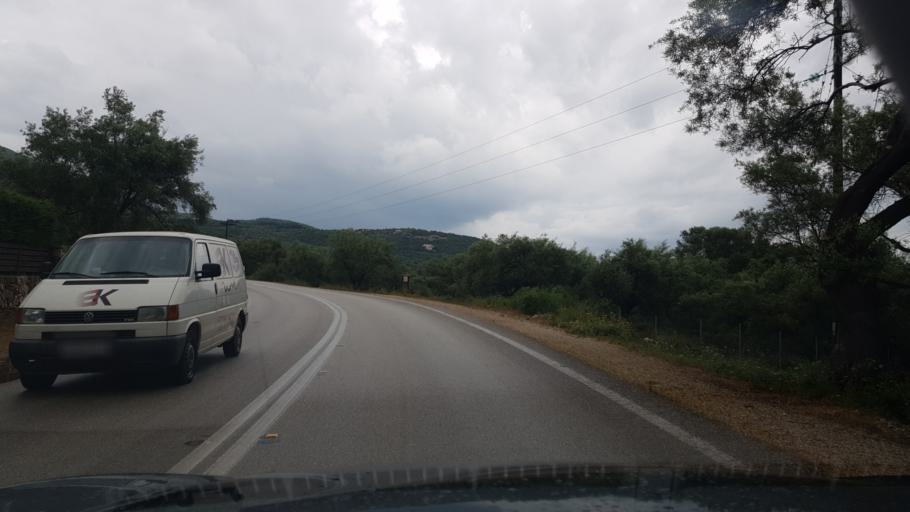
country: GR
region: Ionian Islands
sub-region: Lefkada
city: Nidri
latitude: 38.6384
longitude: 20.6746
